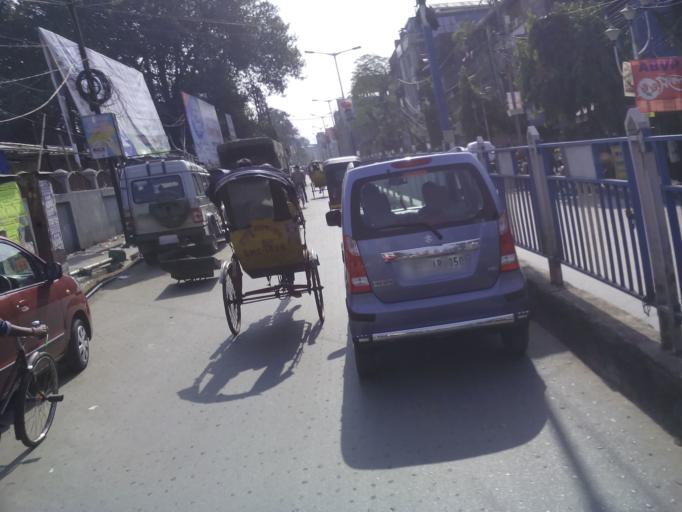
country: IN
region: West Bengal
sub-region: Darjiling
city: Shiliguri
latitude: 26.7144
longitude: 88.4262
